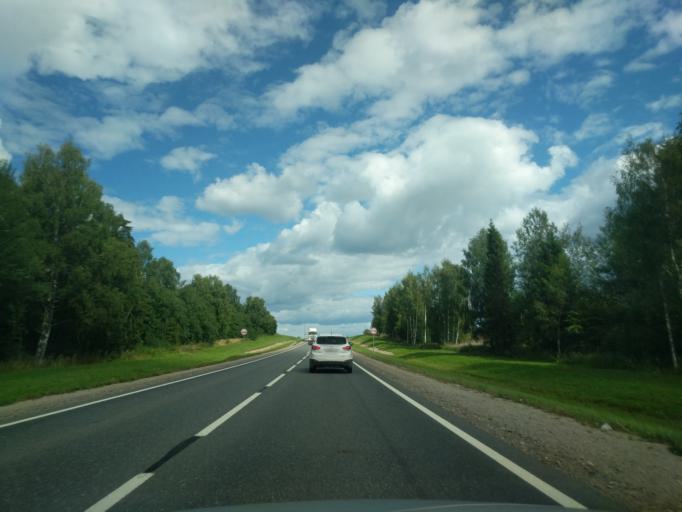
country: RU
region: Kostroma
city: Oktyabr'skiy
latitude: 57.7955
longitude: 41.1754
